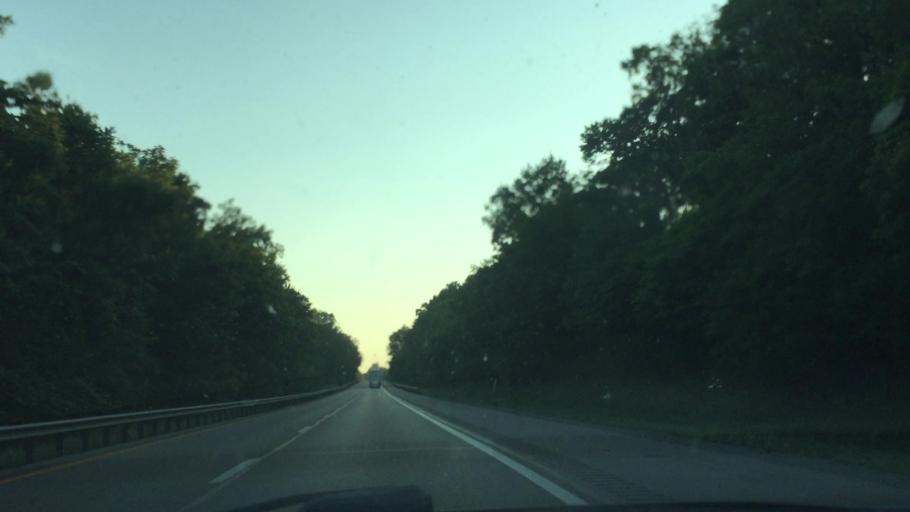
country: US
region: Indiana
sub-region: Switzerland County
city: Vevay
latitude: 38.6766
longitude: -84.9946
